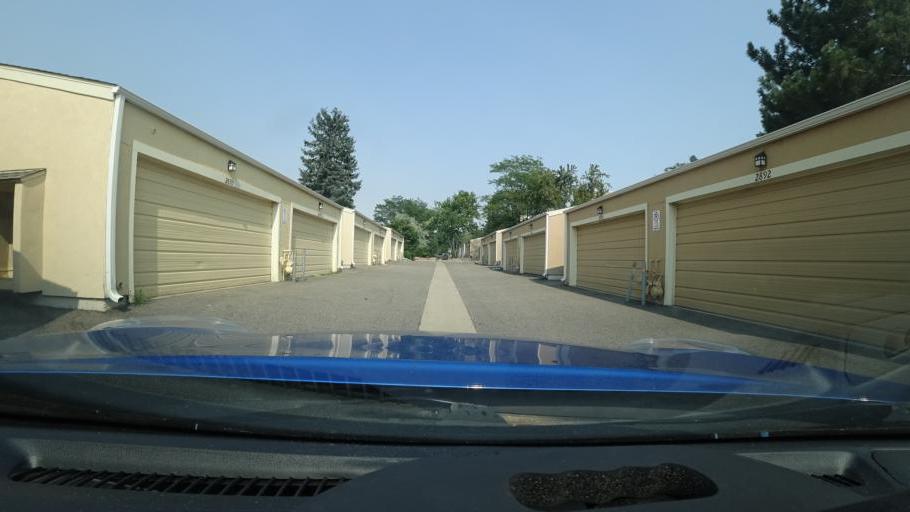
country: US
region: Colorado
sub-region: Adams County
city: Aurora
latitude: 39.6643
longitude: -104.8373
